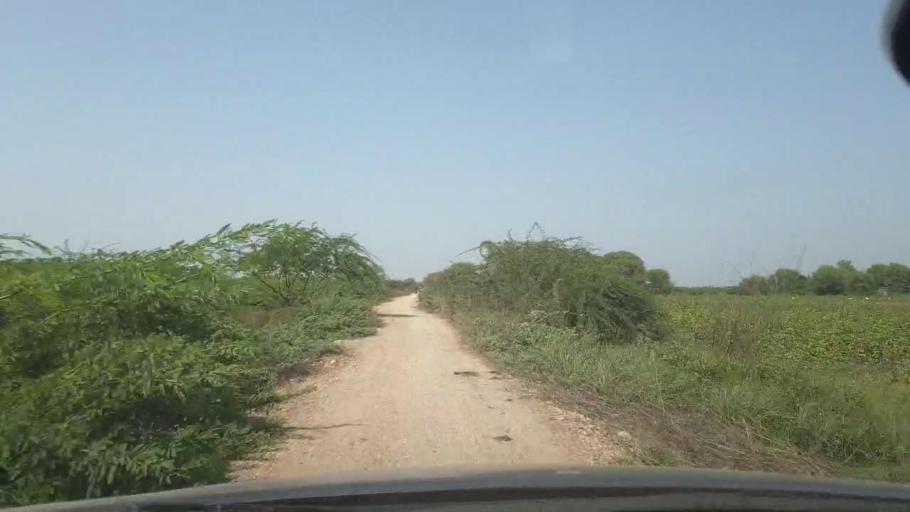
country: PK
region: Sindh
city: Naukot
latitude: 24.7973
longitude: 69.2410
